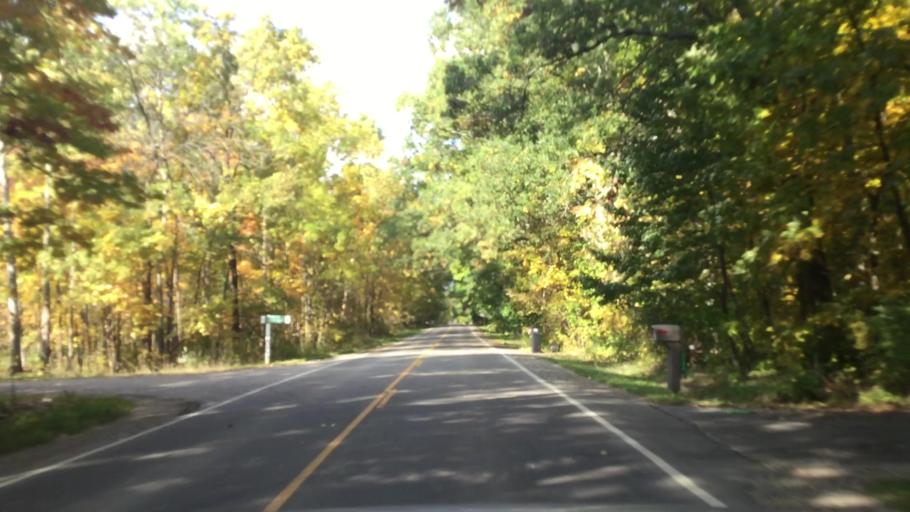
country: US
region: Michigan
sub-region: Oakland County
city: Milford
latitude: 42.6688
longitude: -83.7015
